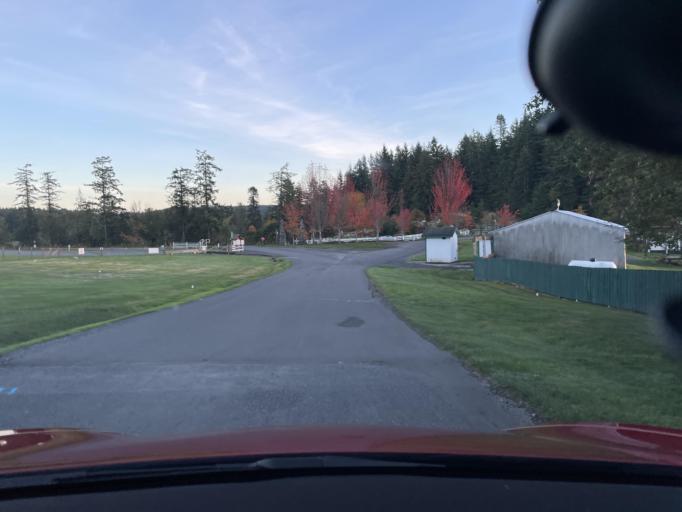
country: US
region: Washington
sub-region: San Juan County
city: Friday Harbor
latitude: 48.6113
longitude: -123.1480
